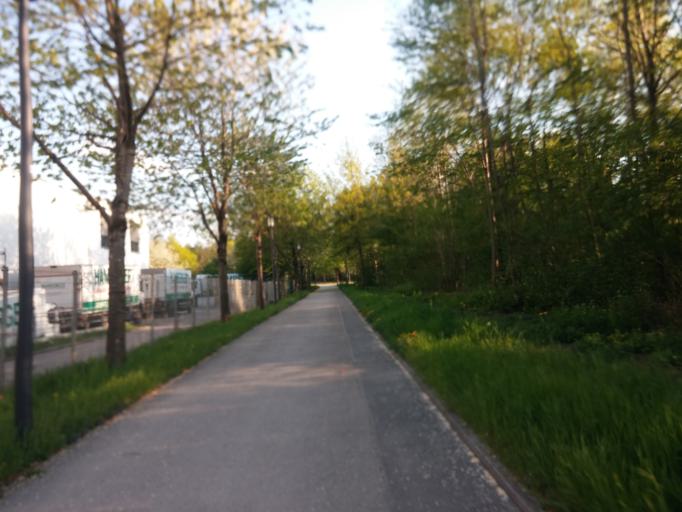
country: DE
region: Bavaria
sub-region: Upper Bavaria
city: Feldkirchen
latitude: 48.1347
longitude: 11.7112
